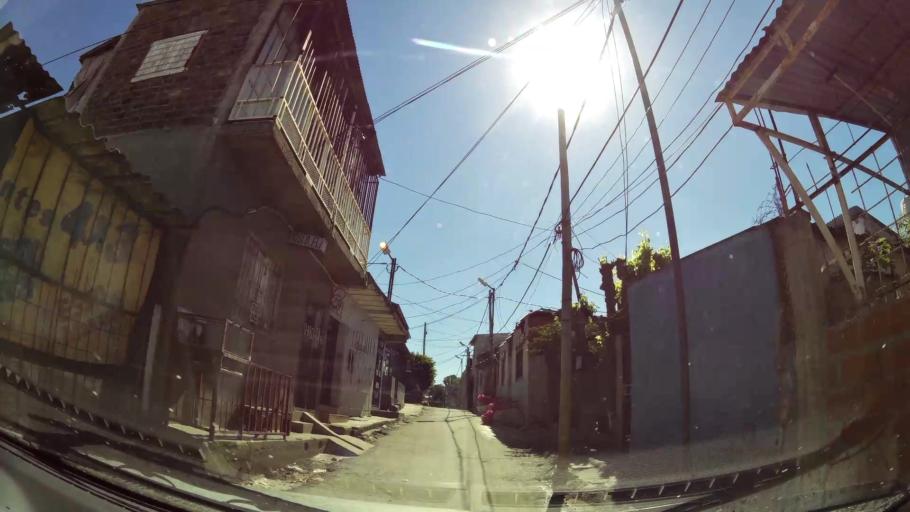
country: AR
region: Buenos Aires
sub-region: Partido de Quilmes
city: Quilmes
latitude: -34.7093
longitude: -58.3031
